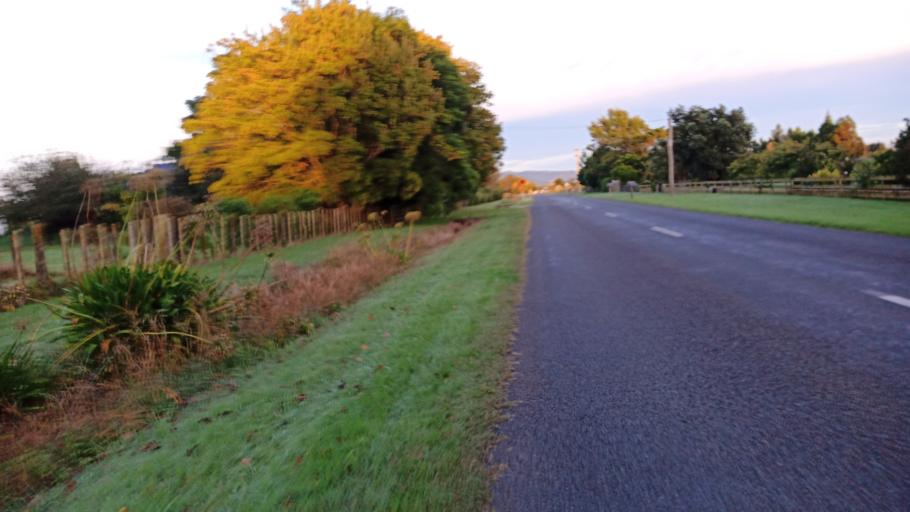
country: NZ
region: Gisborne
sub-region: Gisborne District
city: Gisborne
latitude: -38.6339
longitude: 177.9752
